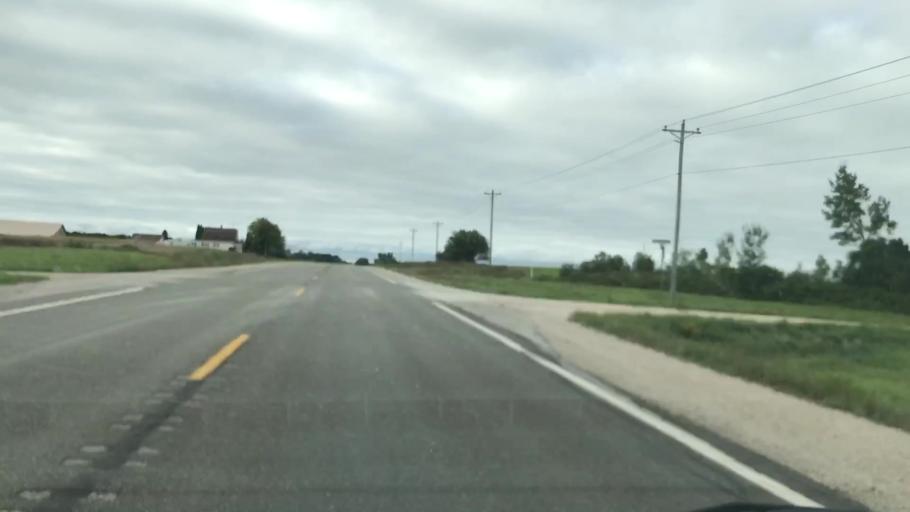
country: US
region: Michigan
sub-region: Luce County
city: Newberry
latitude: 46.1661
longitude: -85.5713
